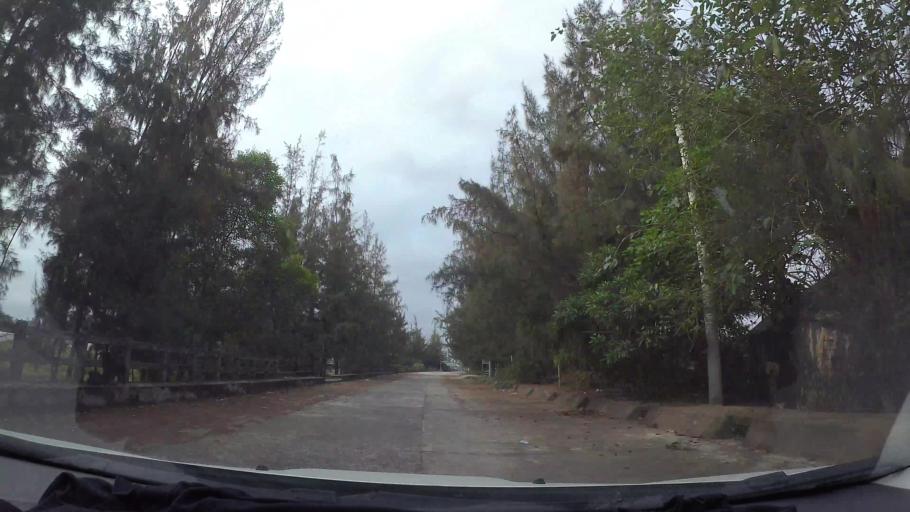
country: VN
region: Da Nang
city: Lien Chieu
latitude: 16.1245
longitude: 108.1237
